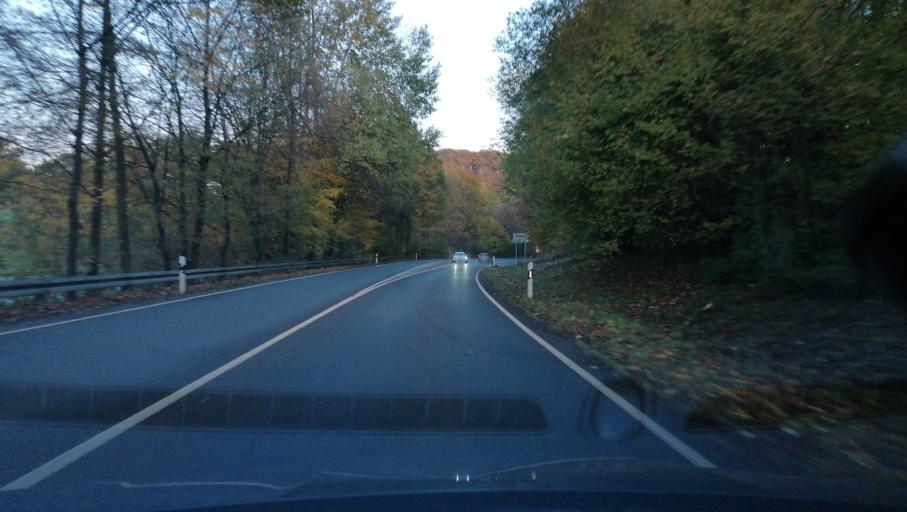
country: DE
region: North Rhine-Westphalia
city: Herdecke
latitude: 51.4146
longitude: 7.4214
